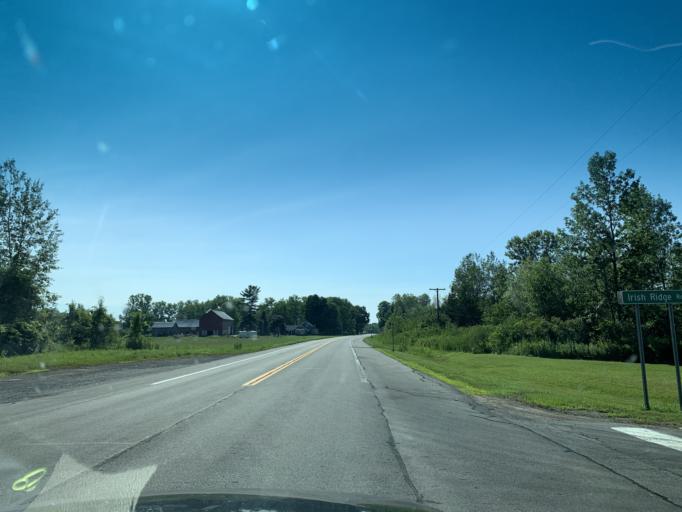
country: US
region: New York
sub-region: Madison County
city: Oneida
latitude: 43.1452
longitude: -75.6520
